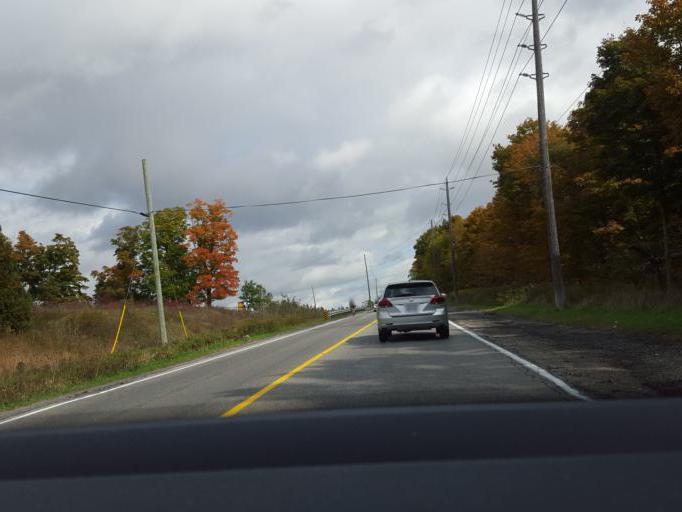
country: CA
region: Ontario
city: Markham
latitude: 43.8489
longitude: -79.1975
